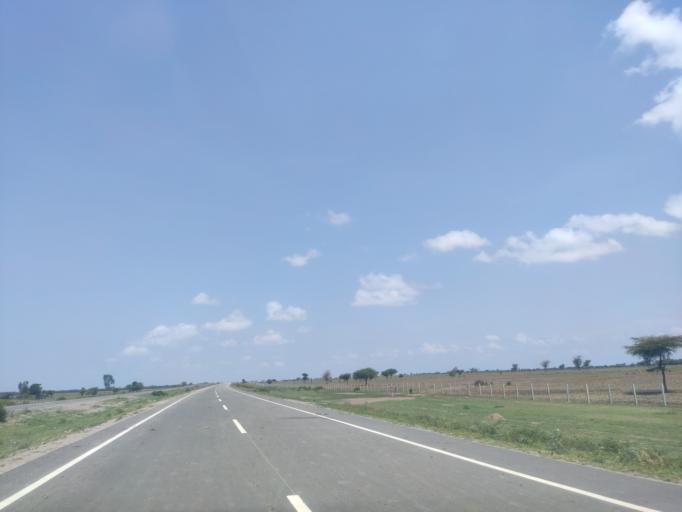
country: ET
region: Oromiya
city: Ziway
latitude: 8.2300
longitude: 38.8723
